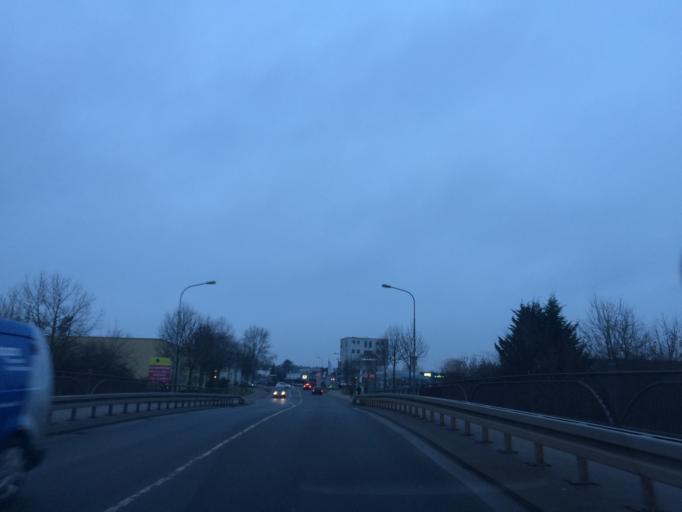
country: DE
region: Hesse
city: Langen
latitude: 49.9996
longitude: 8.6527
